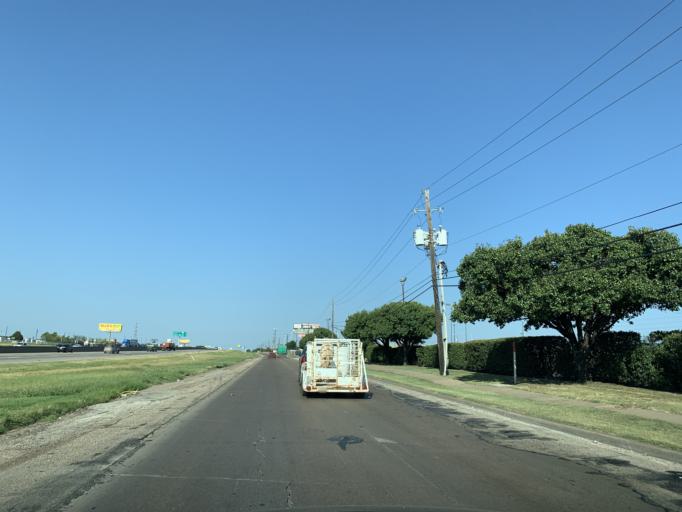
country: US
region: Texas
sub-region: Dallas County
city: Hutchins
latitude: 32.6547
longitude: -96.7556
